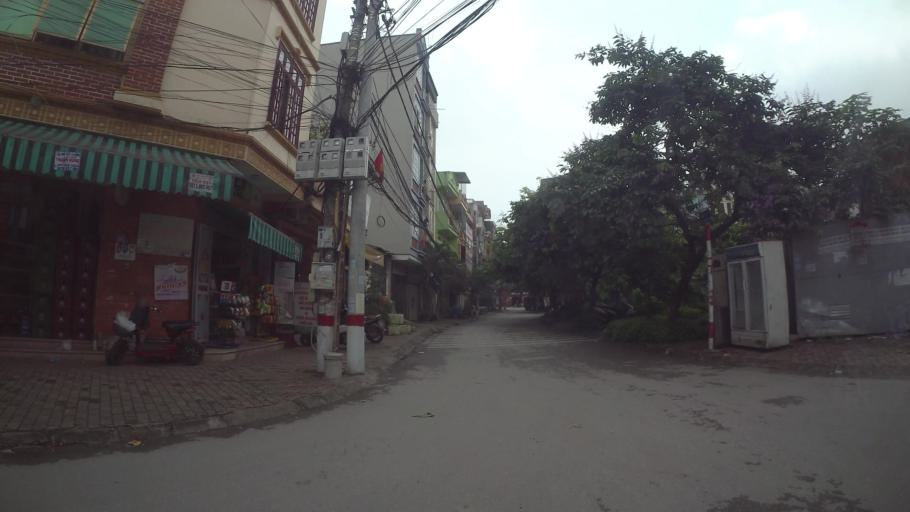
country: VN
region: Ha Noi
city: Van Dien
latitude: 20.9718
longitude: 105.8465
